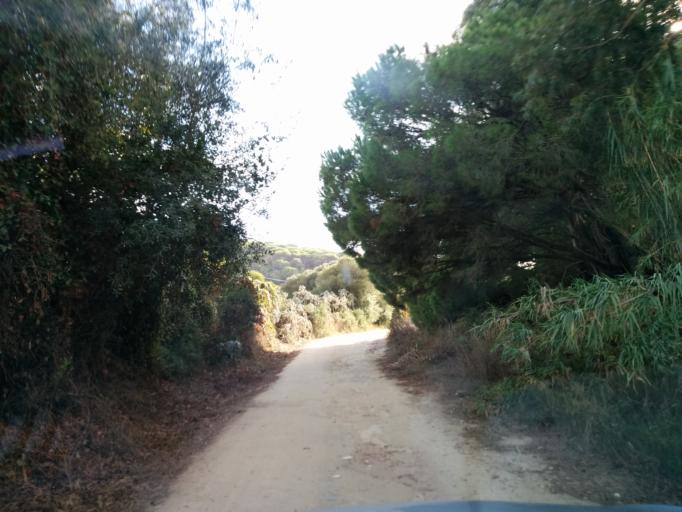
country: ES
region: Andalusia
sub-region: Provincia de Cadiz
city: Vejer de la Frontera
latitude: 36.2105
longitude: -6.0000
